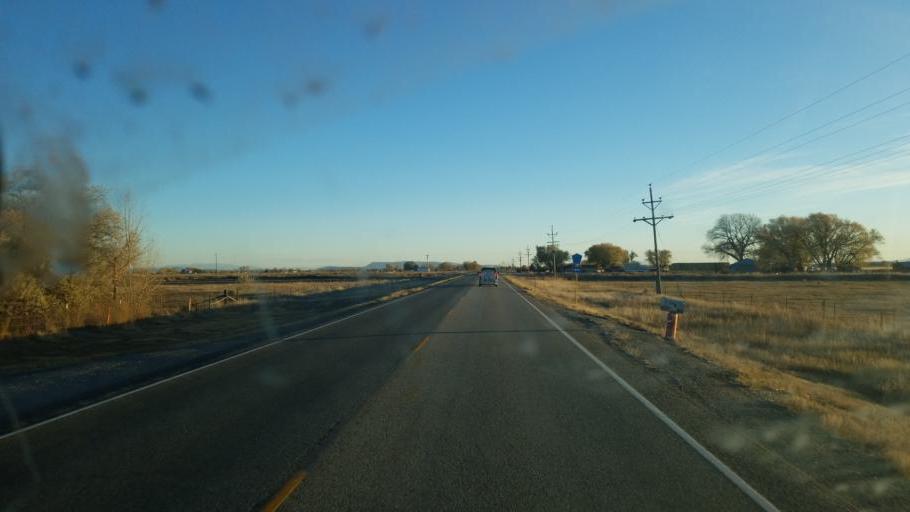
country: US
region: Colorado
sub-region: Alamosa County
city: Alamosa East
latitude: 37.5194
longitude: -105.8579
